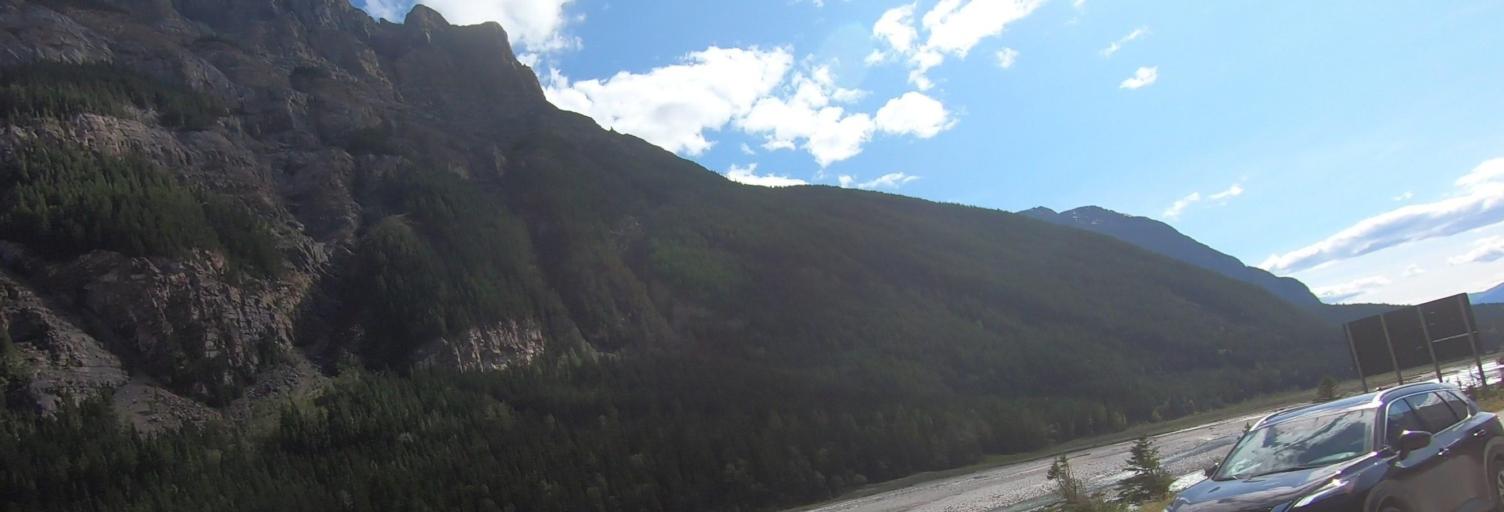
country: CA
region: Alberta
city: Lake Louise
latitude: 51.4143
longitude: -116.4541
